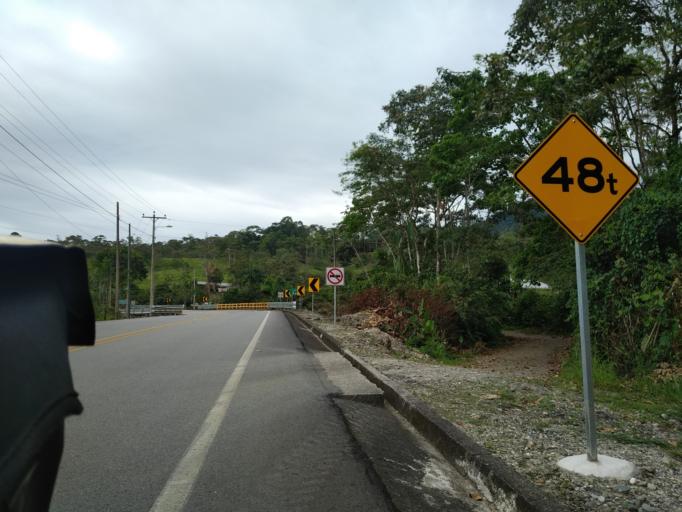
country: EC
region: Napo
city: Tena
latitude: -1.2455
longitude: -77.8779
